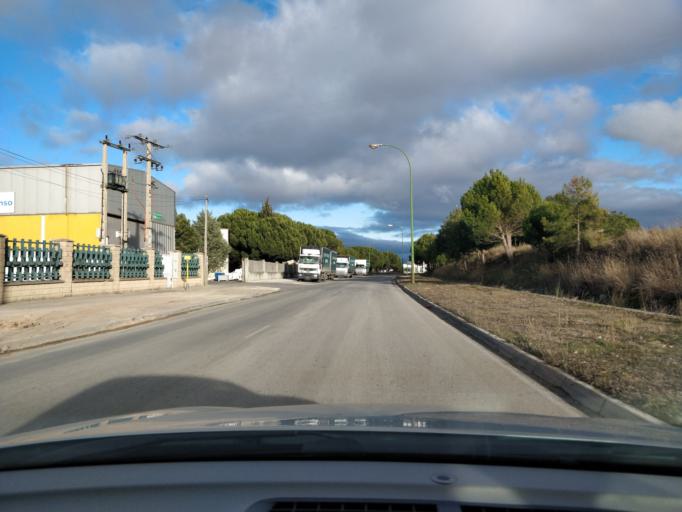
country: ES
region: Castille and Leon
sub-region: Provincia de Burgos
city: Villalbilla de Burgos
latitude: 42.3641
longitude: -3.7465
